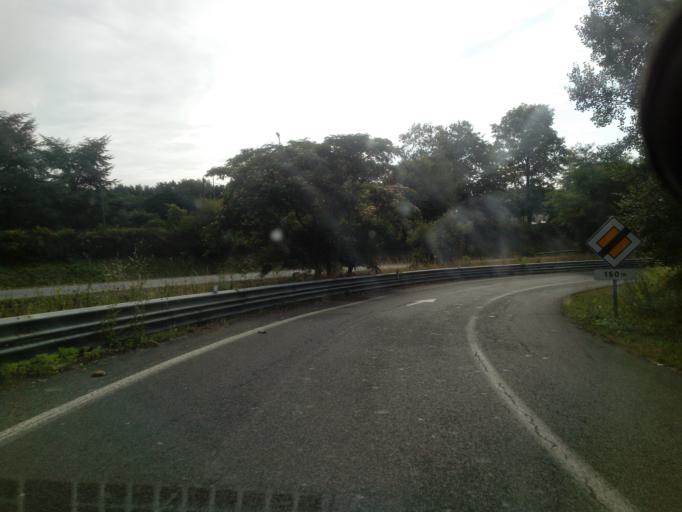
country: FR
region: Pays de la Loire
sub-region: Departement de la Loire-Atlantique
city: Orvault
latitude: 47.2669
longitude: -1.5873
